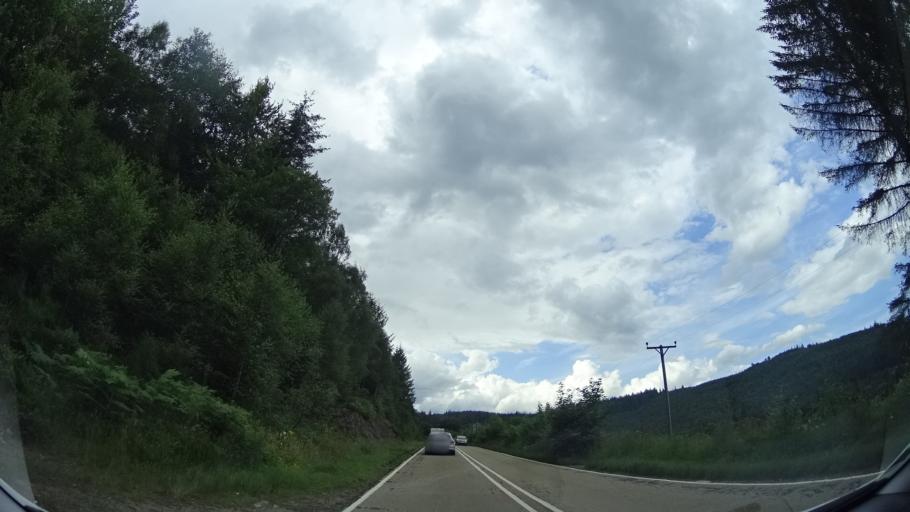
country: GB
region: Scotland
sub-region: Highland
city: Spean Bridge
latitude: 57.0654
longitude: -4.7843
